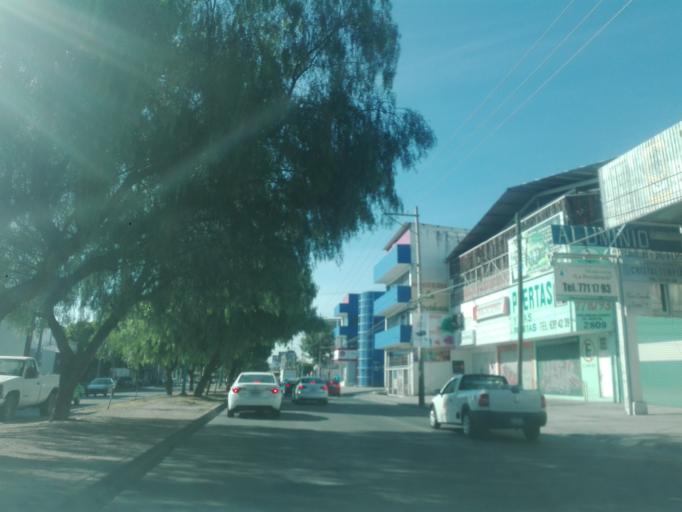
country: MX
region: Guanajuato
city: Leon
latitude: 21.1063
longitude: -101.6559
